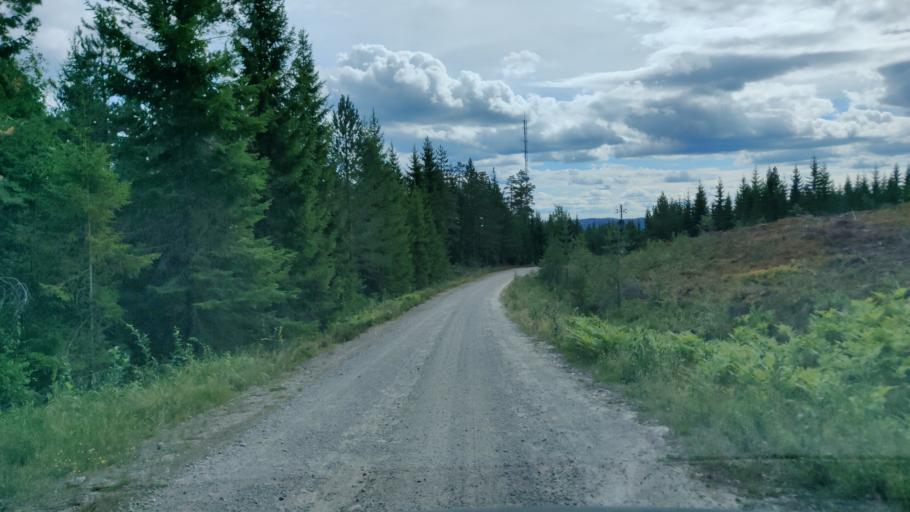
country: SE
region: Vaermland
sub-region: Hagfors Kommun
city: Hagfors
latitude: 60.0183
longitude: 13.7308
